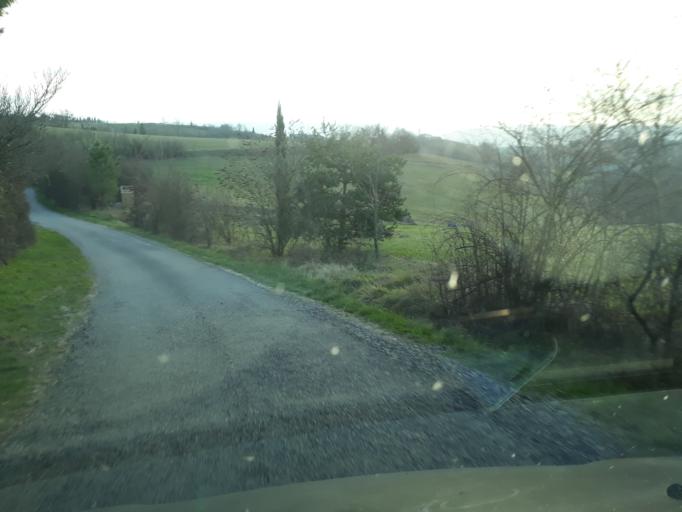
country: FR
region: Midi-Pyrenees
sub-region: Departement de la Haute-Garonne
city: Montesquieu-Volvestre
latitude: 43.1765
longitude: 1.3216
